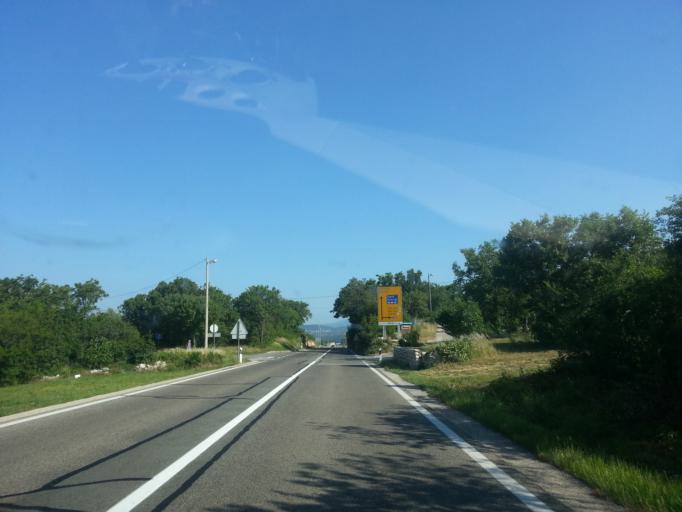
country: HR
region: Primorsko-Goranska
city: Hreljin
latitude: 45.2557
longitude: 14.5939
